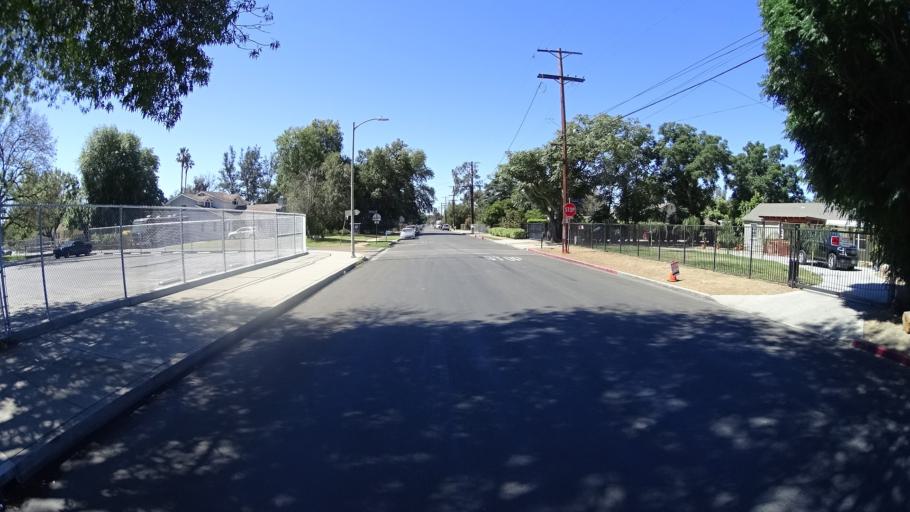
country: US
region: California
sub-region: Los Angeles County
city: San Fernando
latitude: 34.2467
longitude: -118.4609
